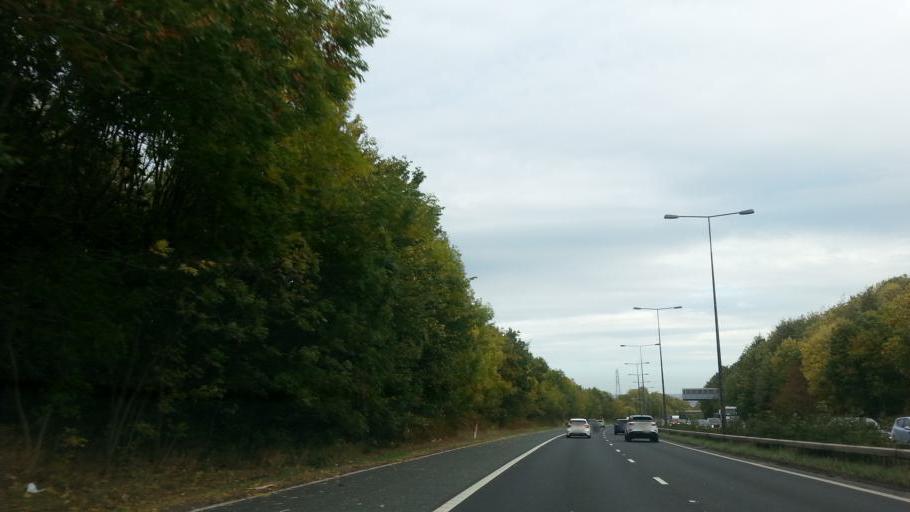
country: GB
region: England
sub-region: City and Borough of Leeds
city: Gildersome
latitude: 53.7559
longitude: -1.6124
